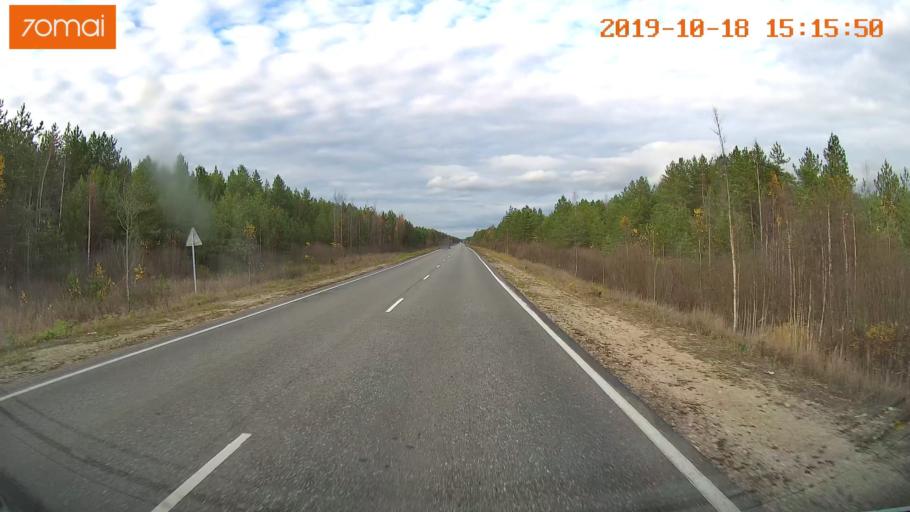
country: RU
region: Vladimir
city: Gus'-Khrustal'nyy
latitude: 55.6255
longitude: 40.7232
